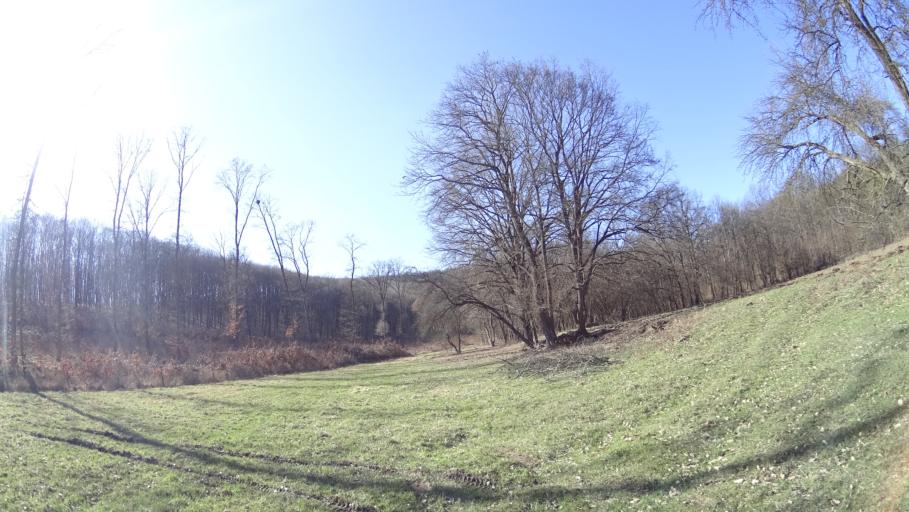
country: HU
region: Pest
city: Veroce
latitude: 47.8669
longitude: 19.0651
